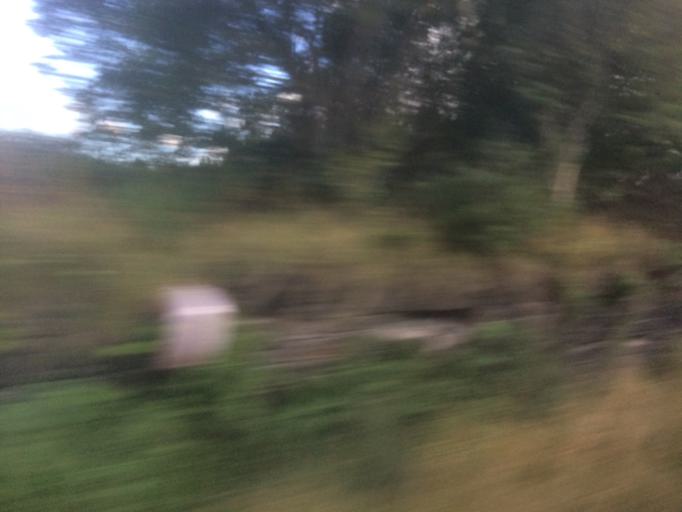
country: GB
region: Scotland
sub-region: North Lanarkshire
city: Kilsyth
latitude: 55.9578
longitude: -4.0332
